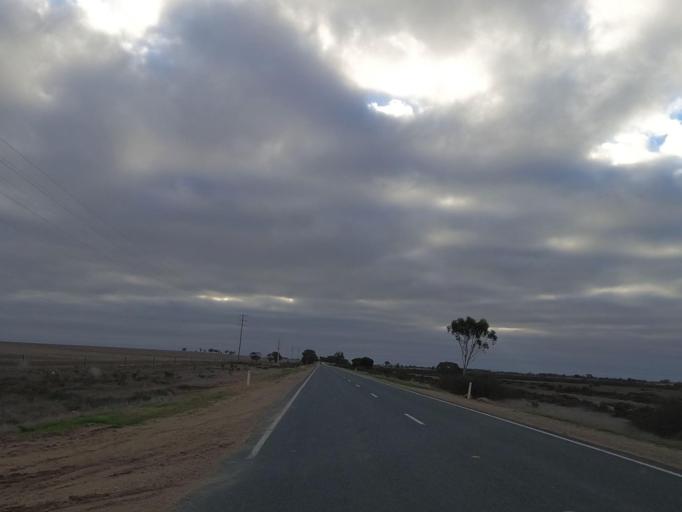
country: AU
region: Victoria
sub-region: Swan Hill
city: Swan Hill
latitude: -35.6386
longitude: 143.8264
